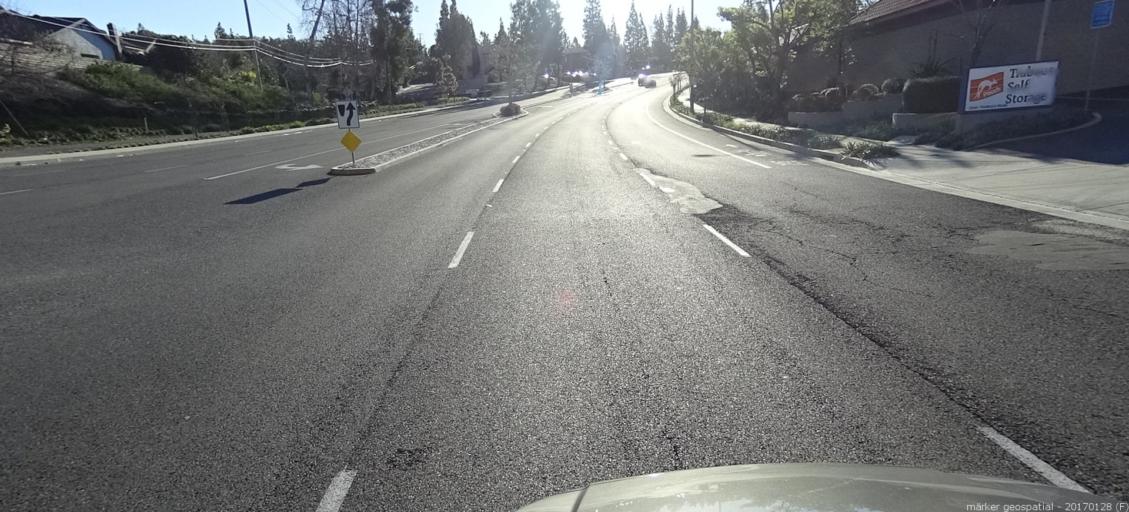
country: US
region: California
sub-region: Orange County
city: Lake Forest
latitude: 33.6493
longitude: -117.6885
